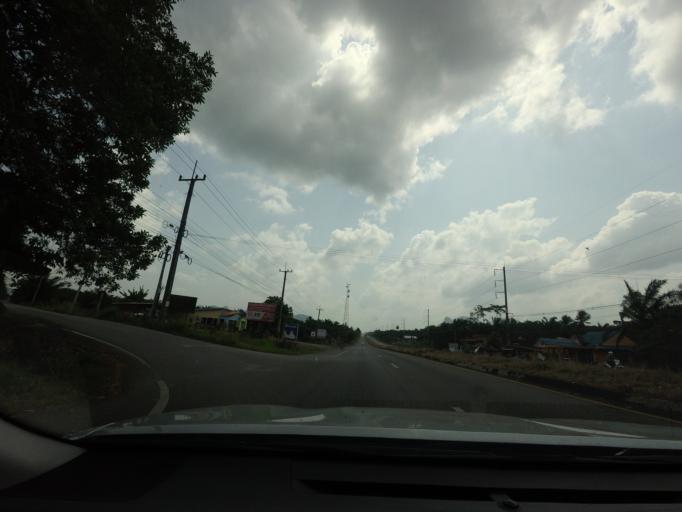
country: TH
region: Phangnga
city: Thap Put
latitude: 8.5027
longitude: 98.6969
